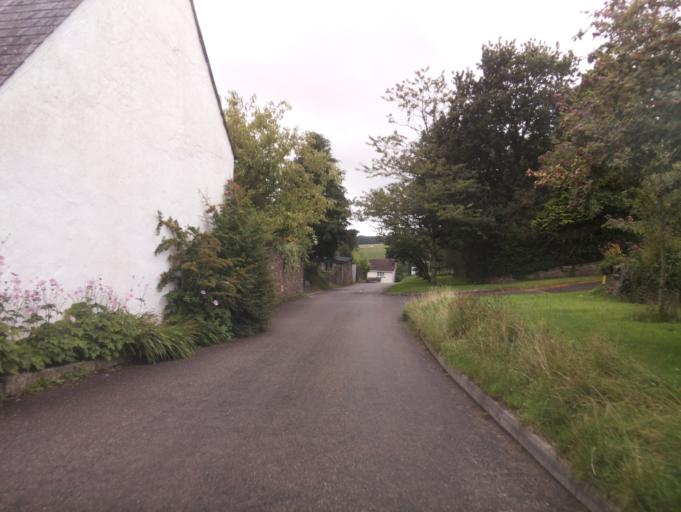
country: GB
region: England
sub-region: Devon
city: Totnes
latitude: 50.3449
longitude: -3.6815
